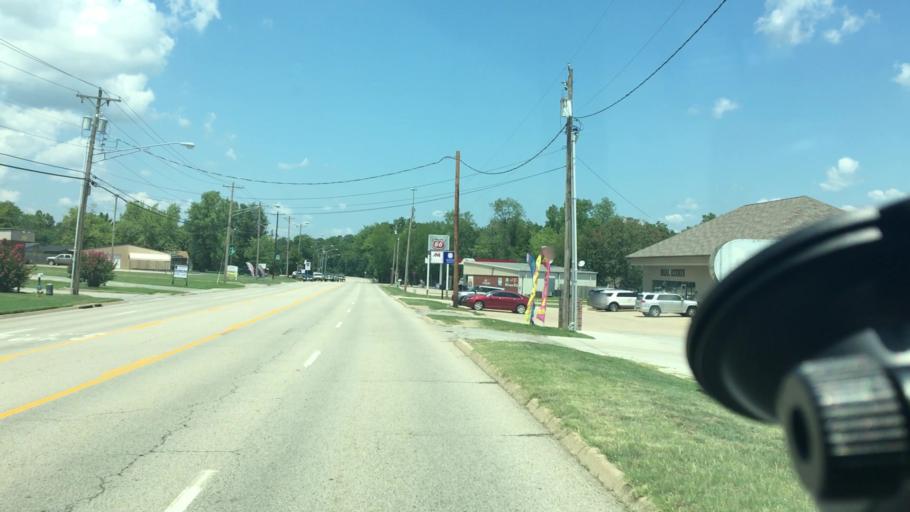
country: US
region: Arkansas
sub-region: Sebastian County
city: Barling
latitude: 35.3316
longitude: -94.3088
